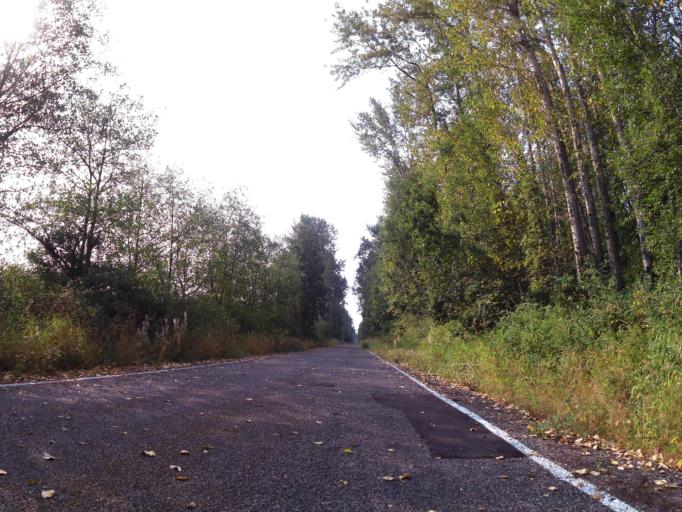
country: US
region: Washington
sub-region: Whatcom County
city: Birch Bay
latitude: 48.8733
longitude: -122.7318
